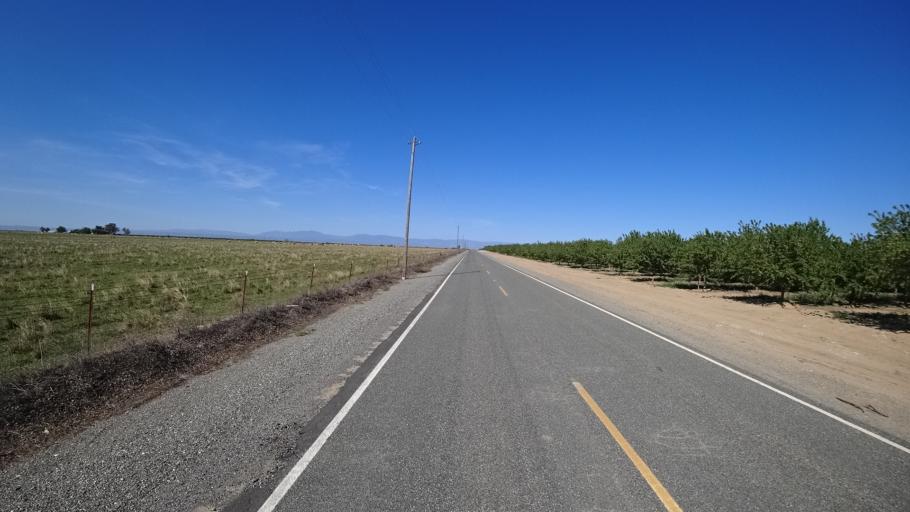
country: US
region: California
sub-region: Glenn County
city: Willows
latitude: 39.6238
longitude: -122.1473
